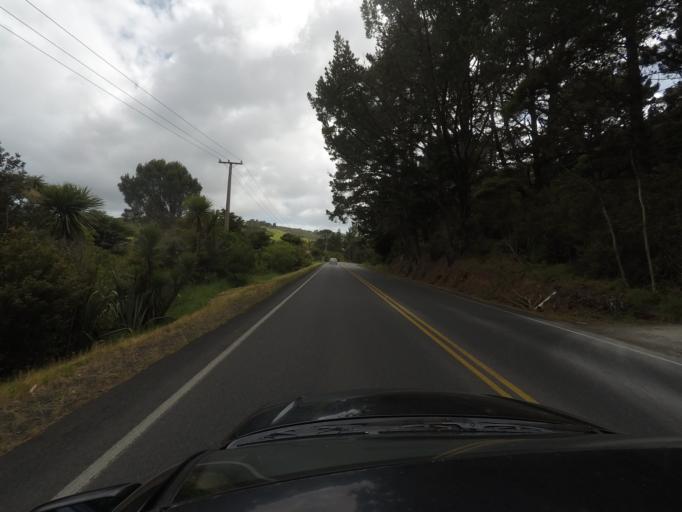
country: NZ
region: Auckland
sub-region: Auckland
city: Warkworth
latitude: -36.5604
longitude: 174.6968
